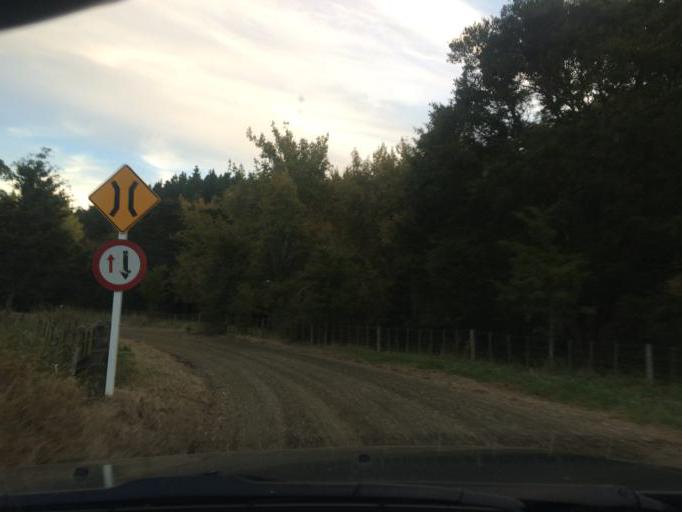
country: NZ
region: Northland
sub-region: Whangarei
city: Maungatapere
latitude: -35.8113
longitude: 174.0371
